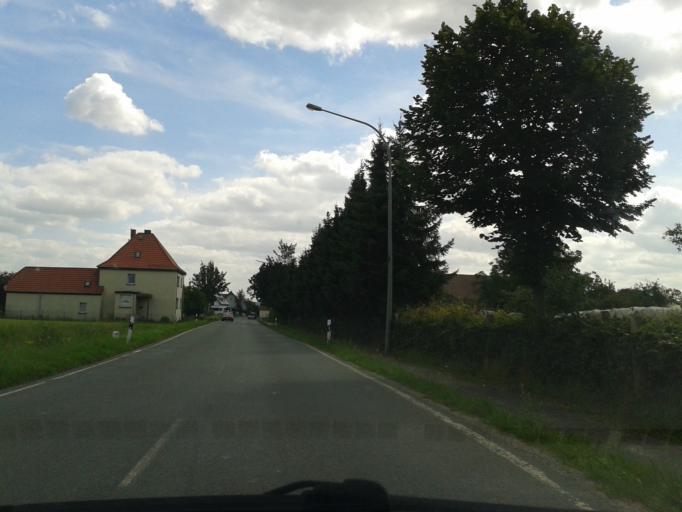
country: DE
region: North Rhine-Westphalia
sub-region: Regierungsbezirk Detmold
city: Schlangen
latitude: 51.8080
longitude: 8.8501
